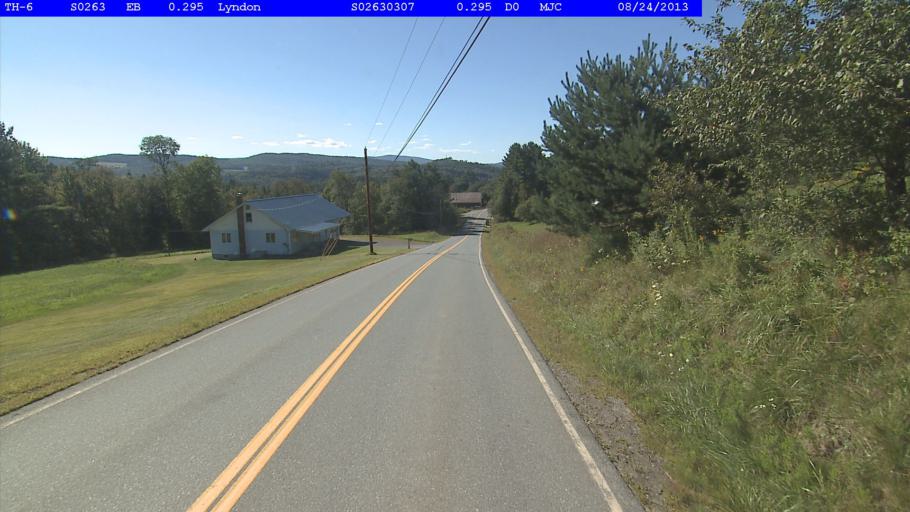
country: US
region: Vermont
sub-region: Caledonia County
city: Lyndon
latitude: 44.4953
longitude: -71.9747
